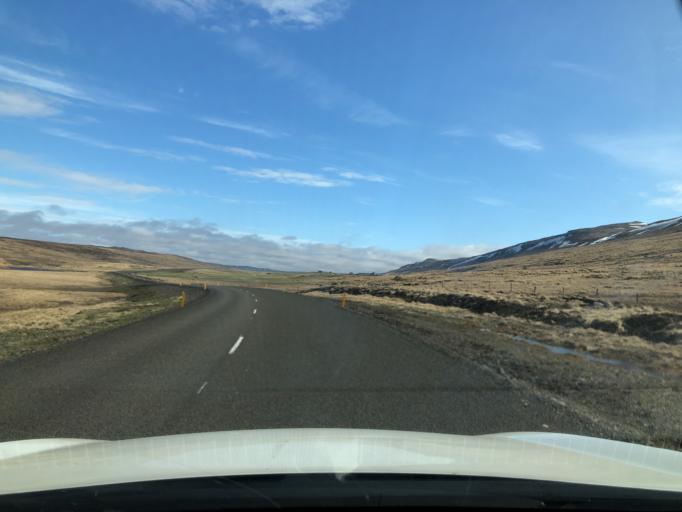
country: IS
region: West
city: Borgarnes
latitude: 65.1395
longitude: -21.5949
